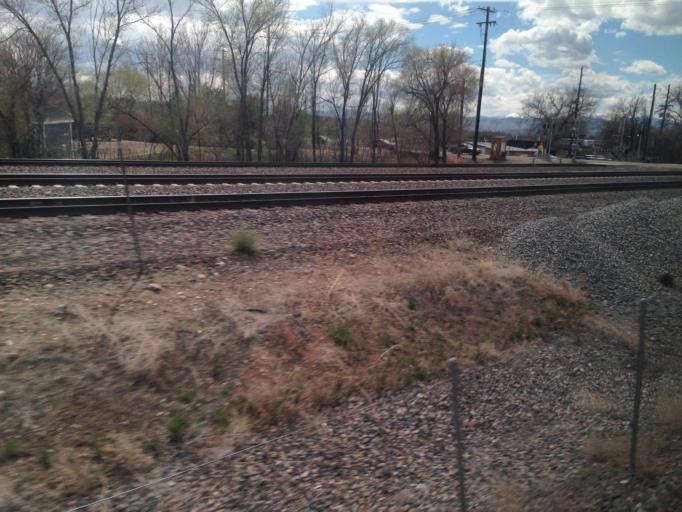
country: US
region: Colorado
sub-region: Adams County
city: Berkley
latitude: 39.8045
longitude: -105.0341
